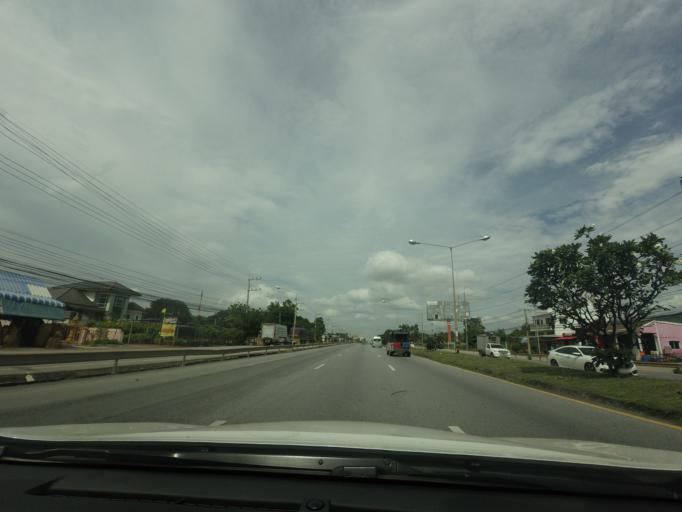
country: TH
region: Sara Buri
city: Muak Lek
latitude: 14.6330
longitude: 101.2383
